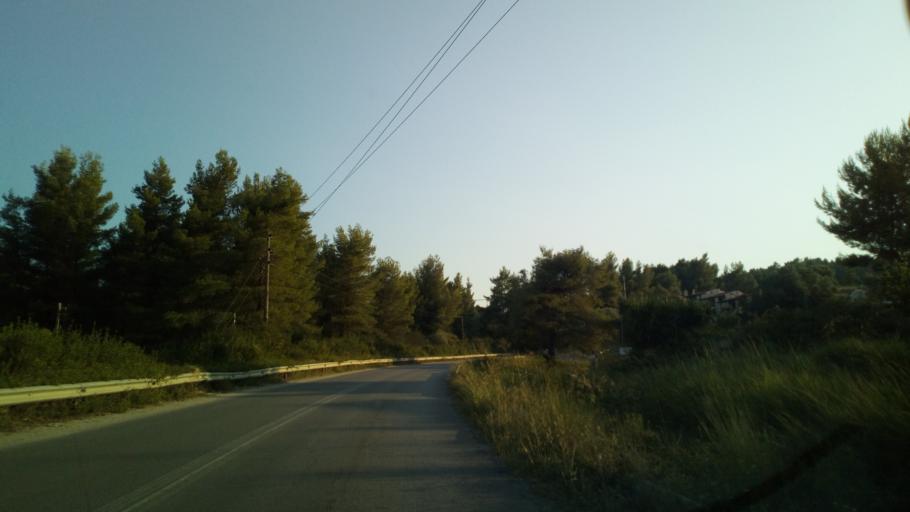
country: GR
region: Central Macedonia
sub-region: Nomos Chalkidikis
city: Pefkochori
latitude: 39.9563
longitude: 23.6745
